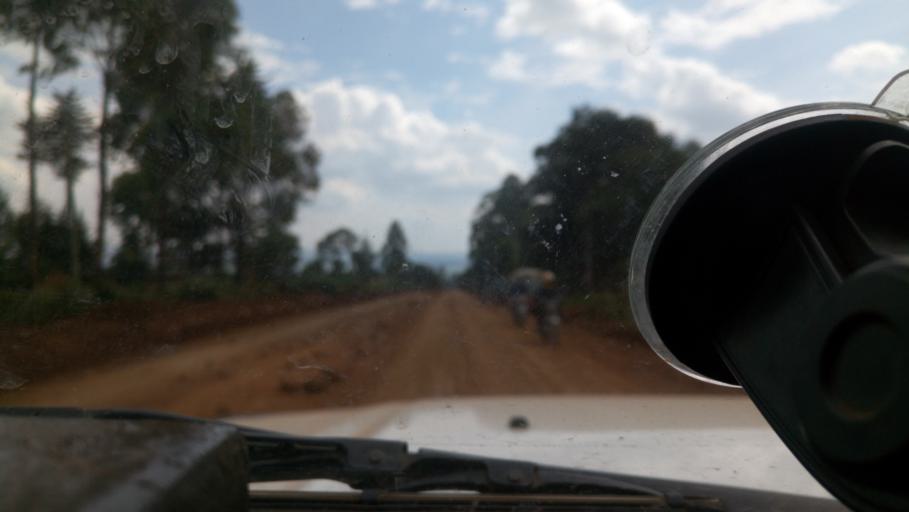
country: KE
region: Kericho
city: Litein
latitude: -0.5822
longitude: 35.1305
